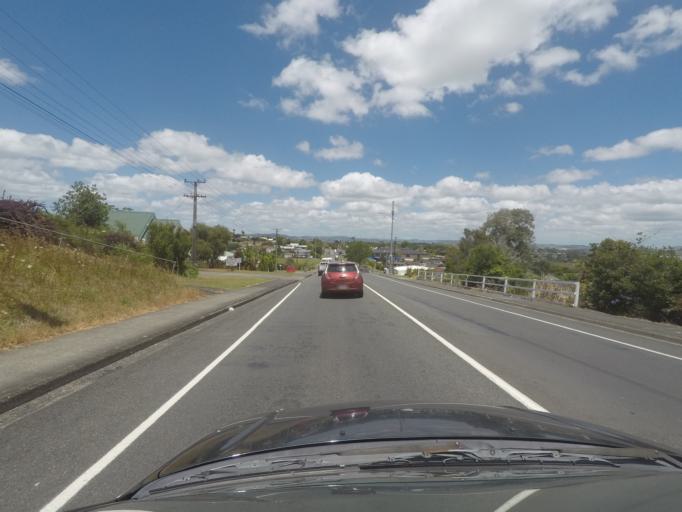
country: NZ
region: Northland
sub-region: Whangarei
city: Whangarei
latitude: -35.7515
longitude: 174.3680
